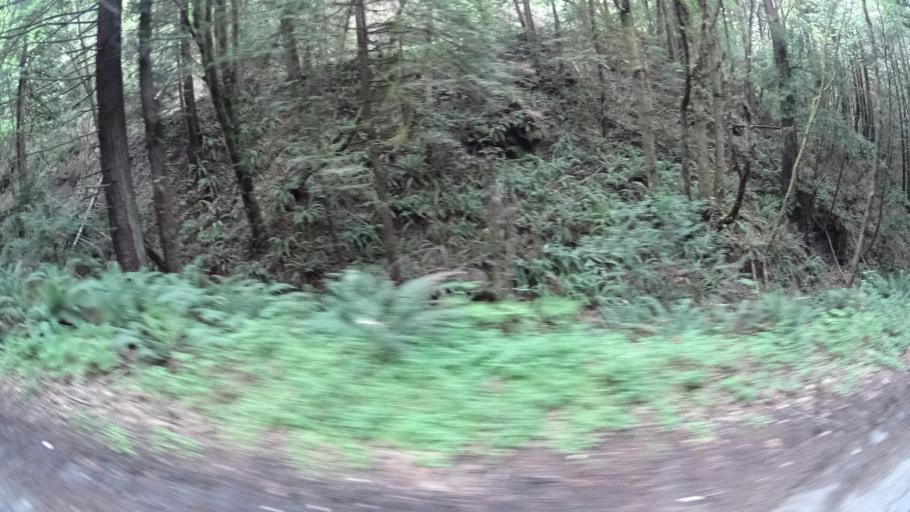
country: US
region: California
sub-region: Humboldt County
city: Redway
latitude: 40.3356
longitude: -123.9035
